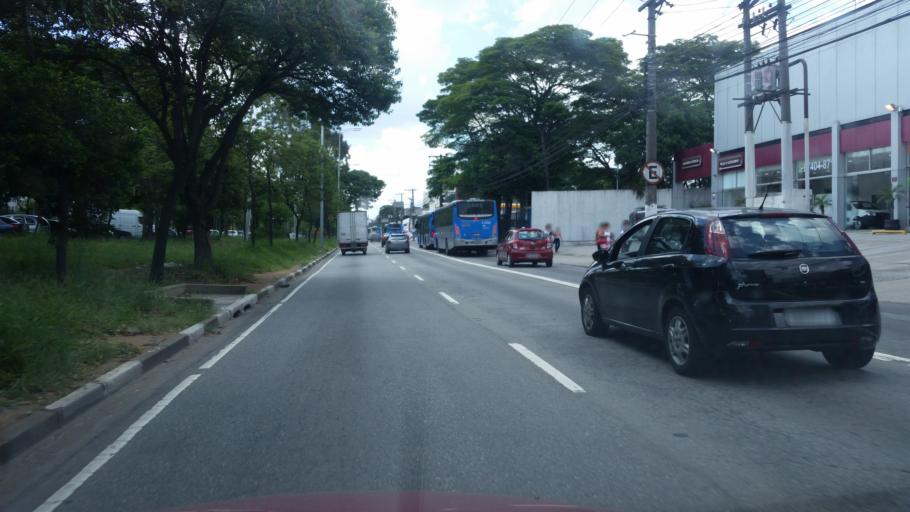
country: BR
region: Sao Paulo
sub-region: Diadema
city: Diadema
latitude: -23.6786
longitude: -46.6964
